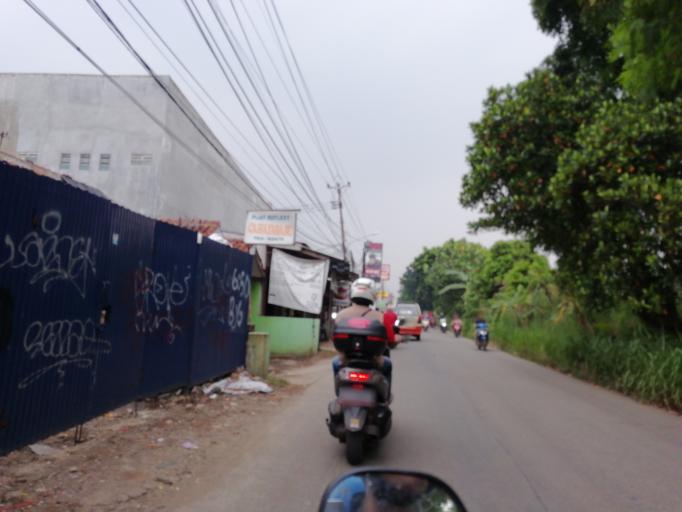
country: ID
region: West Java
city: Cibinong
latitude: -6.4744
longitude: 106.8033
